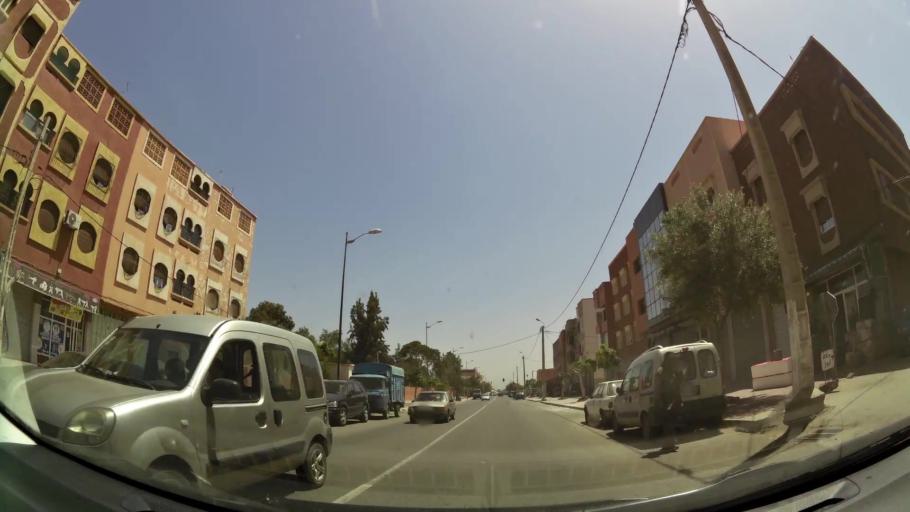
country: MA
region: Souss-Massa-Draa
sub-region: Inezgane-Ait Mellou
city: Inezgane
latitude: 30.3449
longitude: -9.4944
